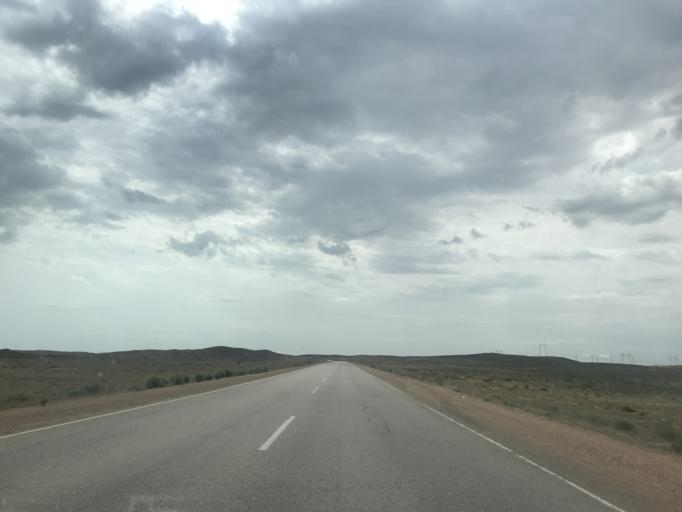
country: KZ
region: Zhambyl
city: Mynaral
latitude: 45.5178
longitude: 73.4912
